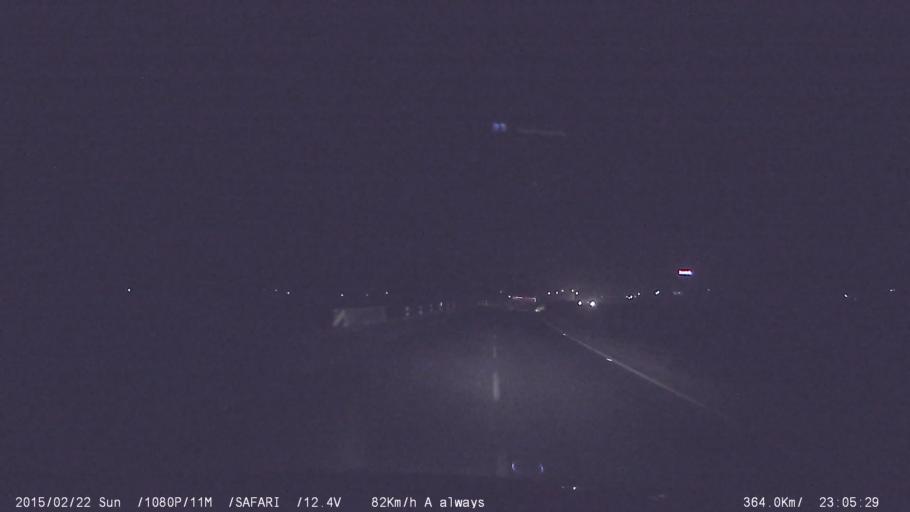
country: IN
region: Tamil Nadu
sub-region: Namakkal
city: Rasipuram
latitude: 11.4154
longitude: 78.1574
